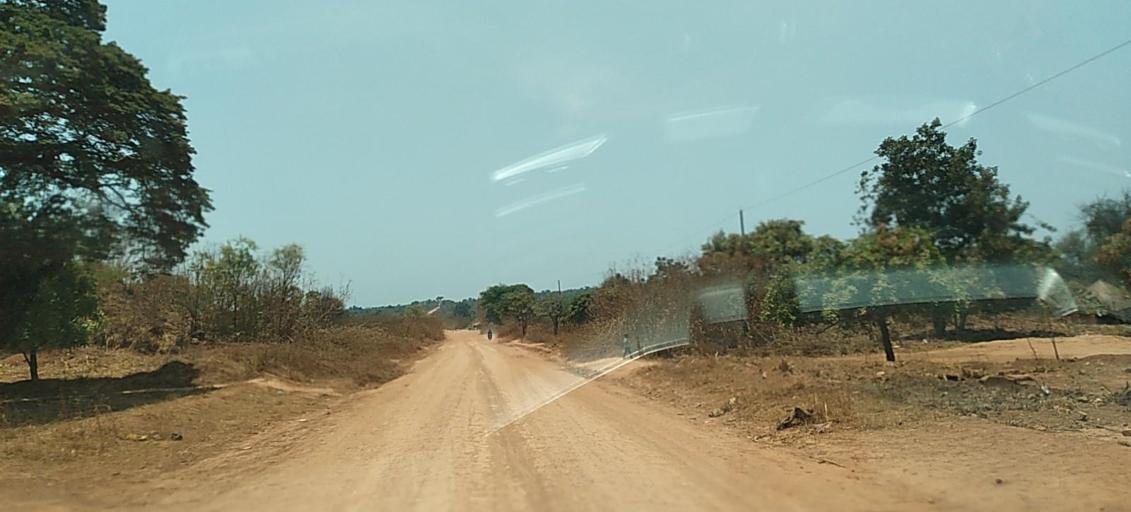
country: CD
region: Katanga
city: Kipushi
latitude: -11.7798
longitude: 27.1899
